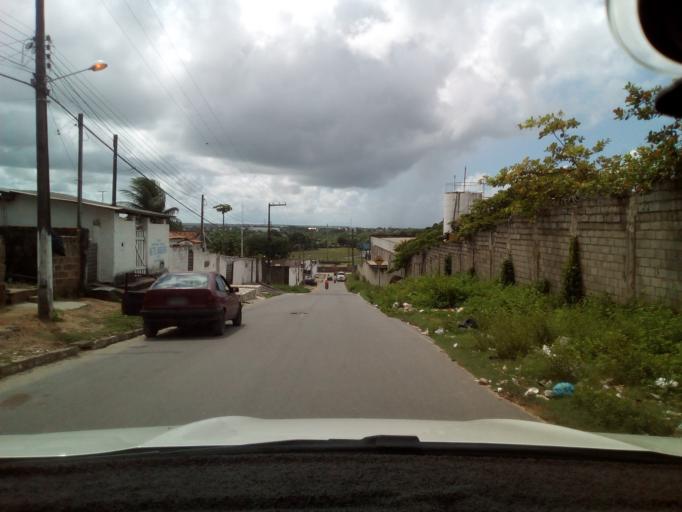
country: BR
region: Paraiba
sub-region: Bayeux
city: Bayeux
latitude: -7.1431
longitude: -34.9224
